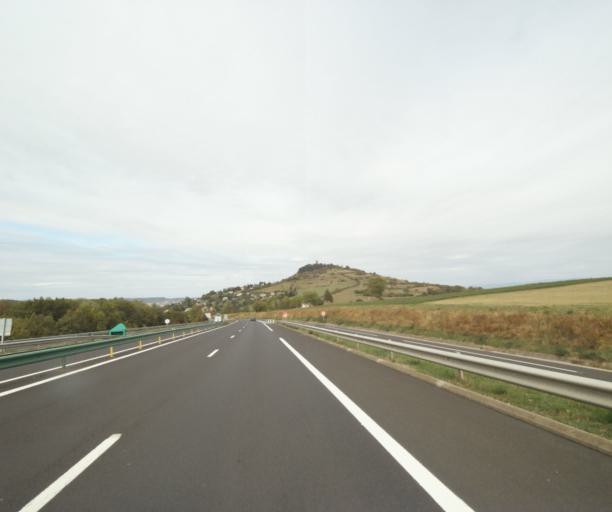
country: FR
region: Auvergne
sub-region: Departement du Puy-de-Dome
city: Ceyrat
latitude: 45.7203
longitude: 3.0708
